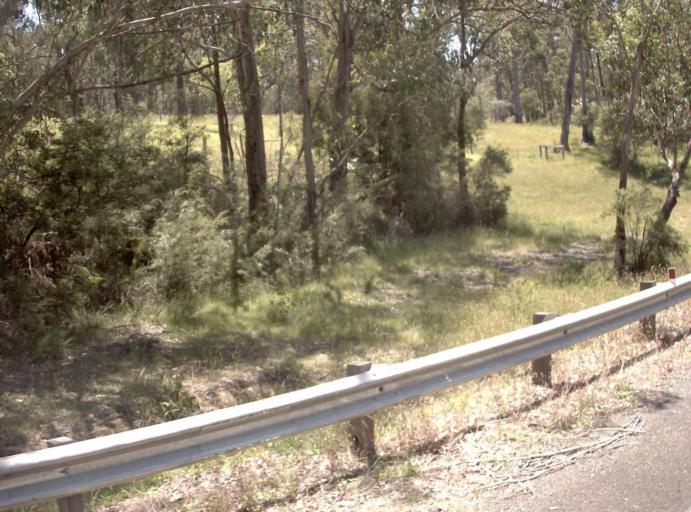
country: AU
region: Victoria
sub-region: East Gippsland
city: Lakes Entrance
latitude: -37.7354
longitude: 148.0826
